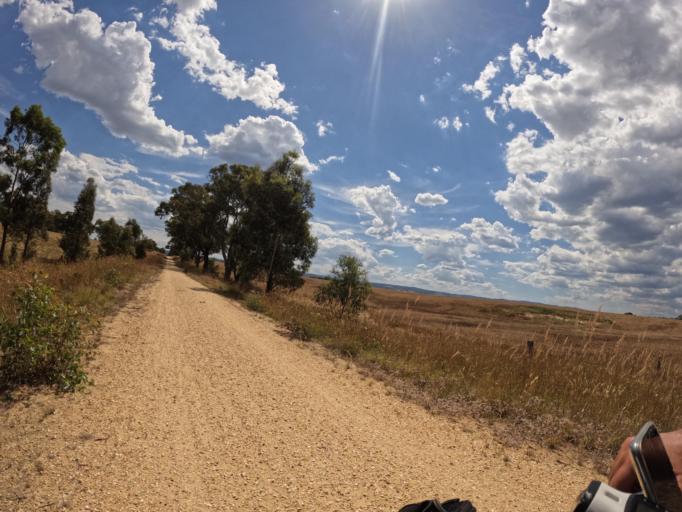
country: AU
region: Victoria
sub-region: Wellington
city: Heyfield
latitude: -37.9786
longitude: 146.7490
